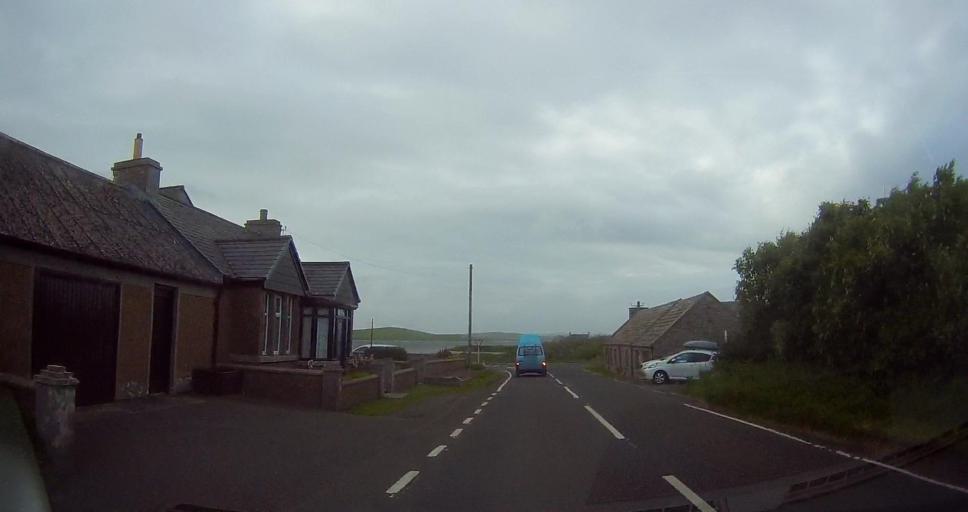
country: GB
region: Scotland
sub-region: Orkney Islands
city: Stromness
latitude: 58.9827
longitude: -3.2470
